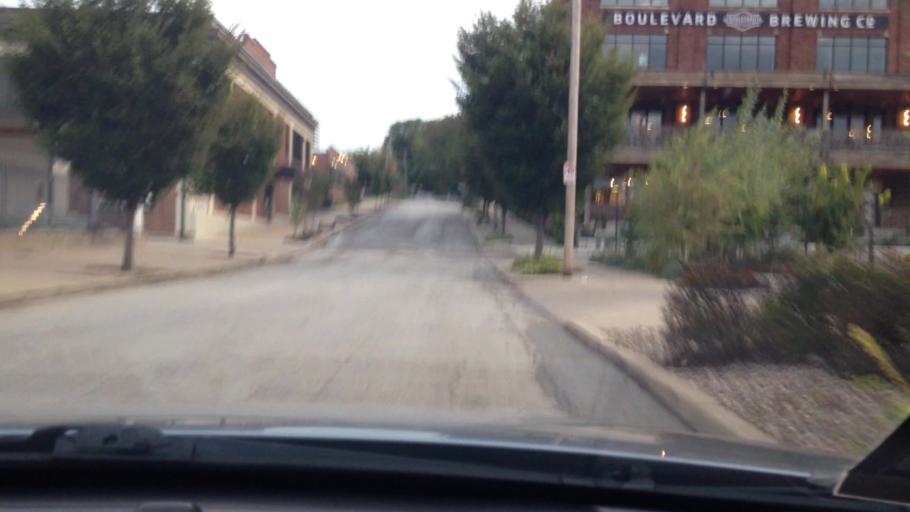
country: US
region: Missouri
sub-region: Jackson County
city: Kansas City
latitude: 39.0819
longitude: -94.5952
